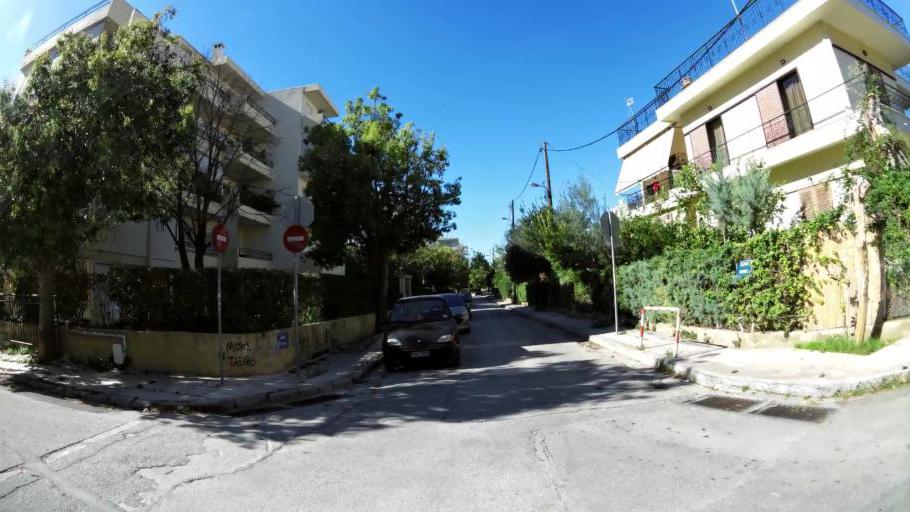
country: GR
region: Attica
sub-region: Nomarchia Athinas
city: Vrilissia
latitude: 38.0238
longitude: 23.8170
